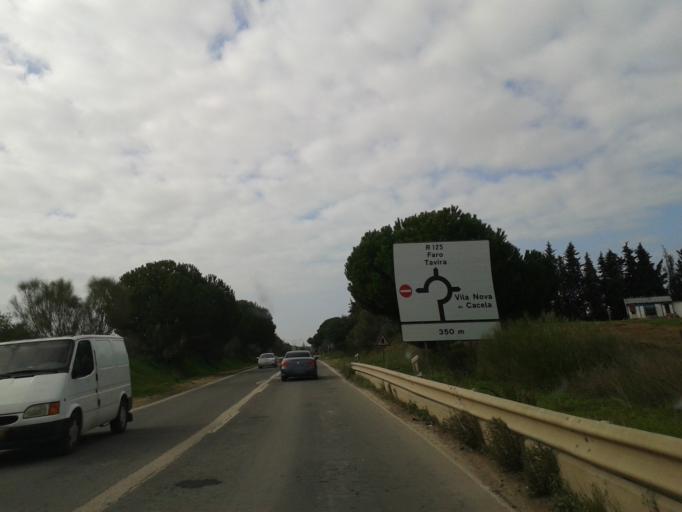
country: PT
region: Faro
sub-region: Vila Real de Santo Antonio
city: Monte Gordo
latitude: 37.1763
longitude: -7.5270
